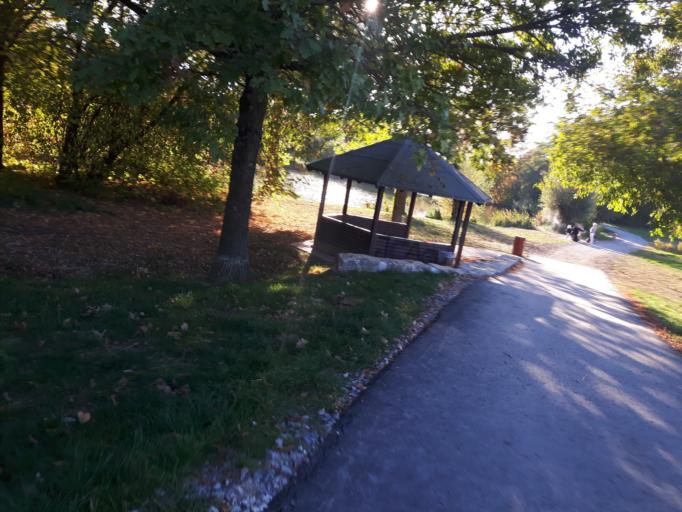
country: DE
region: Baden-Wuerttemberg
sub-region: Regierungsbezirk Stuttgart
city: Untereisesheim
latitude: 49.2103
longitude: 9.1914
